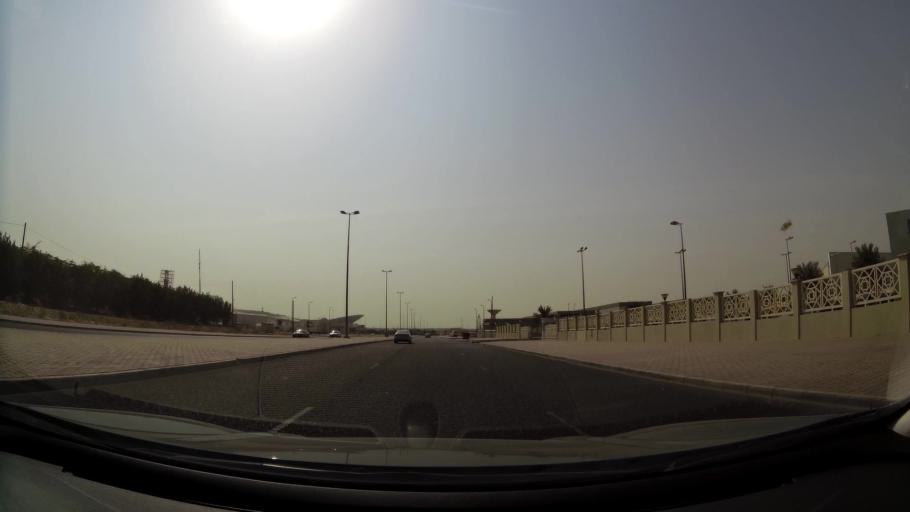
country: KW
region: Al Asimah
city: Ar Rabiyah
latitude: 29.2833
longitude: 47.9145
